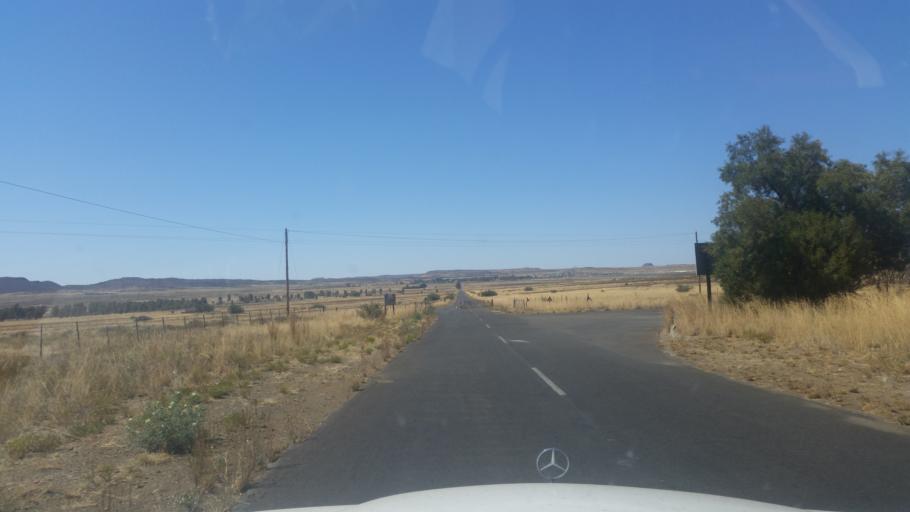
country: ZA
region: Eastern Cape
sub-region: Joe Gqabi District Municipality
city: Burgersdorp
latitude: -30.7462
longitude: 25.7607
